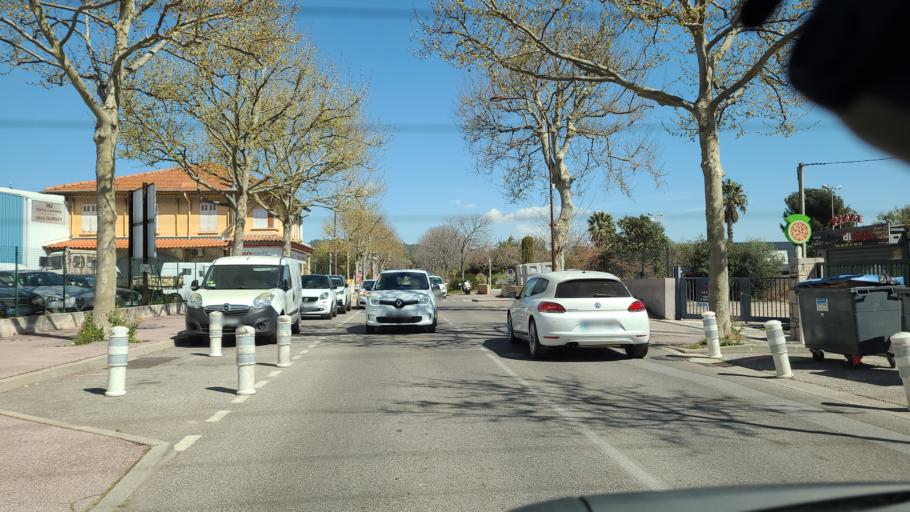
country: FR
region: Provence-Alpes-Cote d'Azur
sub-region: Departement du Var
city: La Valette-du-Var
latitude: 43.1396
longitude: 5.9966
